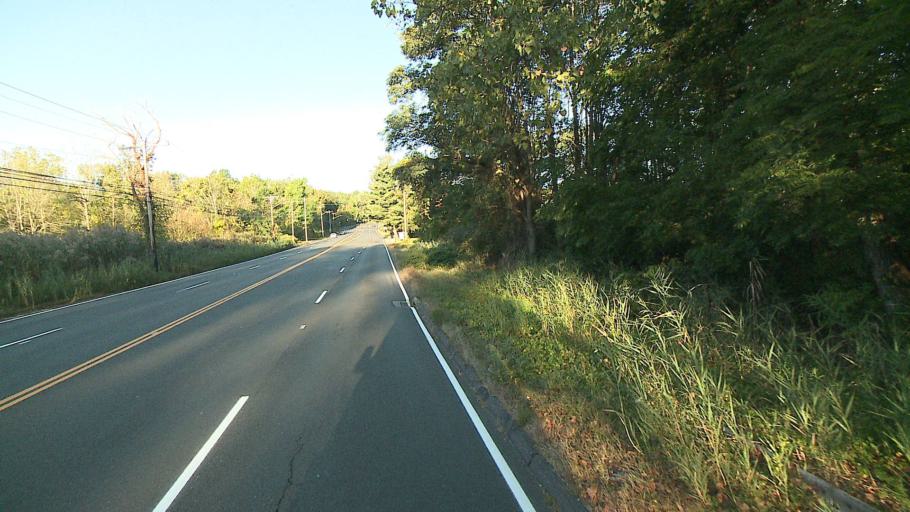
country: US
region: Connecticut
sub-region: Hartford County
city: West Hartford
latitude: 41.7871
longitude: -72.7629
